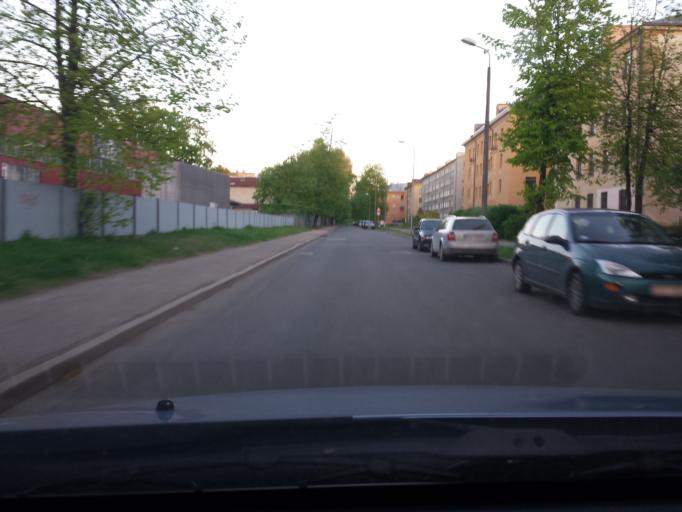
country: LV
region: Riga
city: Riga
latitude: 56.9903
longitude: 24.1340
